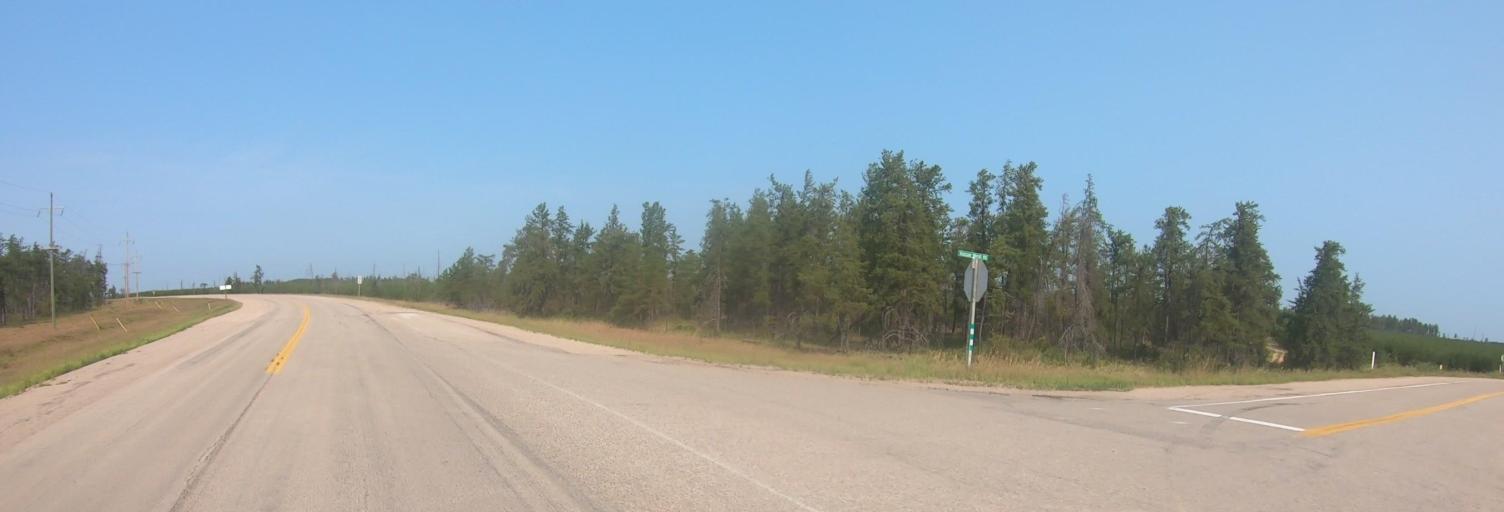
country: US
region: Minnesota
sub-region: Roseau County
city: Roseau
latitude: 49.0886
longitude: -95.8896
